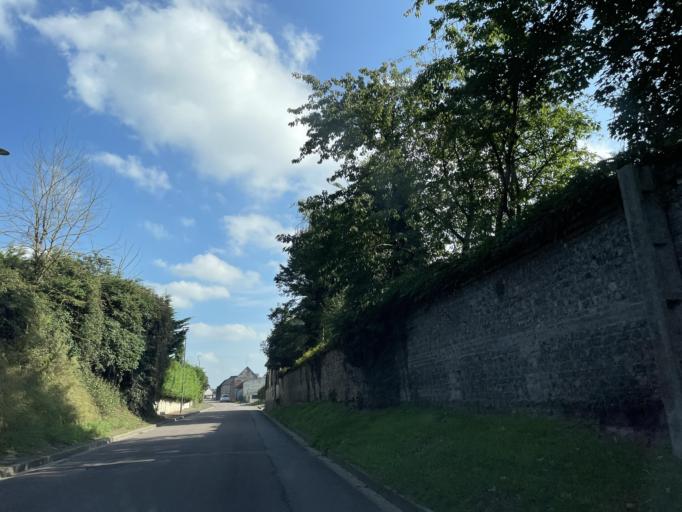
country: FR
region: Haute-Normandie
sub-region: Departement de la Seine-Maritime
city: Criel-sur-Mer
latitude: 50.0394
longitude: 1.3396
